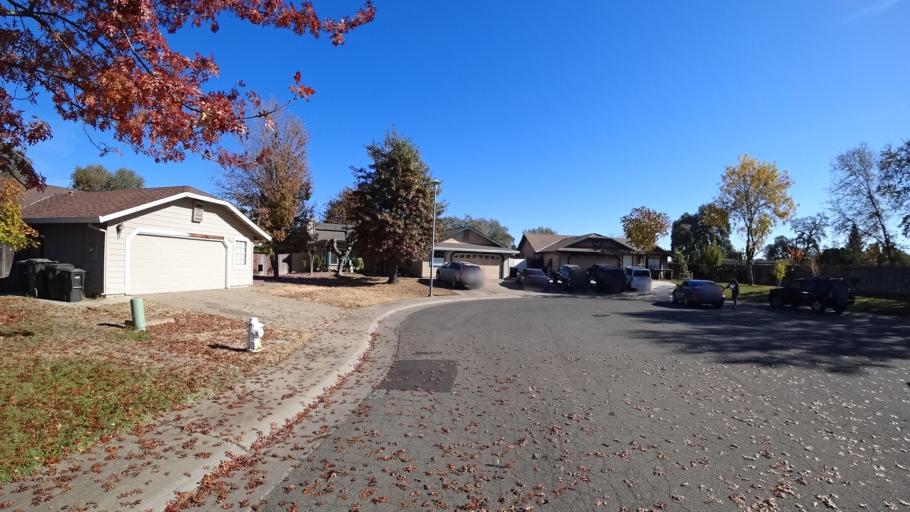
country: US
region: California
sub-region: Sacramento County
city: Antelope
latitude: 38.7223
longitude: -121.3067
